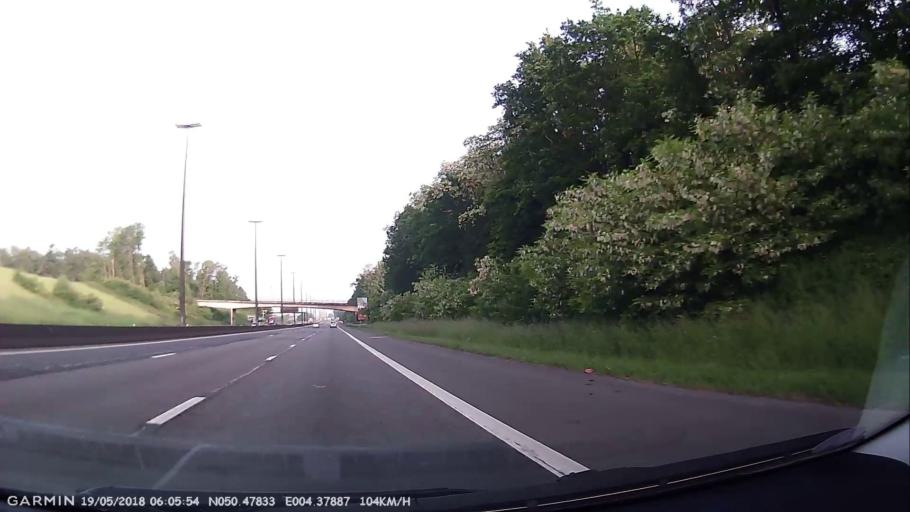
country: BE
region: Wallonia
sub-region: Province du Hainaut
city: Courcelles
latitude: 50.4783
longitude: 4.3786
